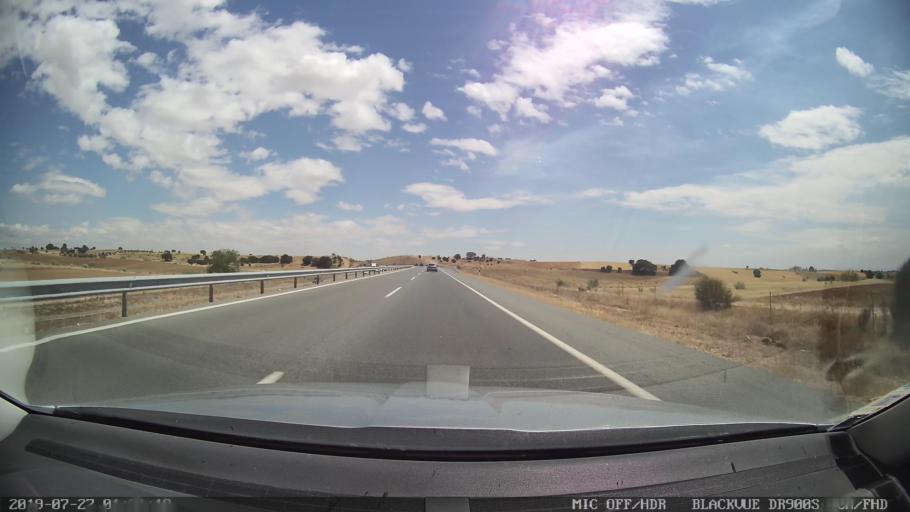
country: ES
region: Castille-La Mancha
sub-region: Province of Toledo
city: Santa Cruz del Retamar
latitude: 40.1165
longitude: -4.2832
